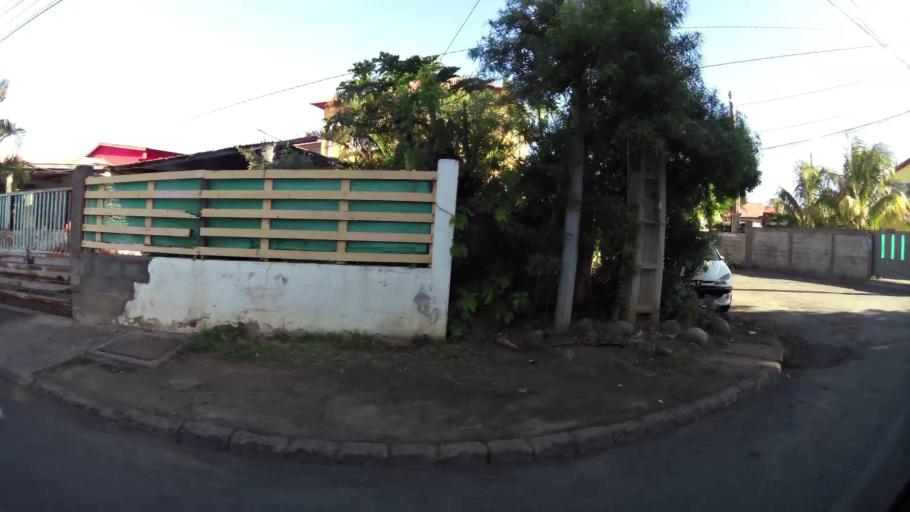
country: RE
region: Reunion
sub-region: Reunion
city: Saint-Louis
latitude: -21.2931
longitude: 55.3944
